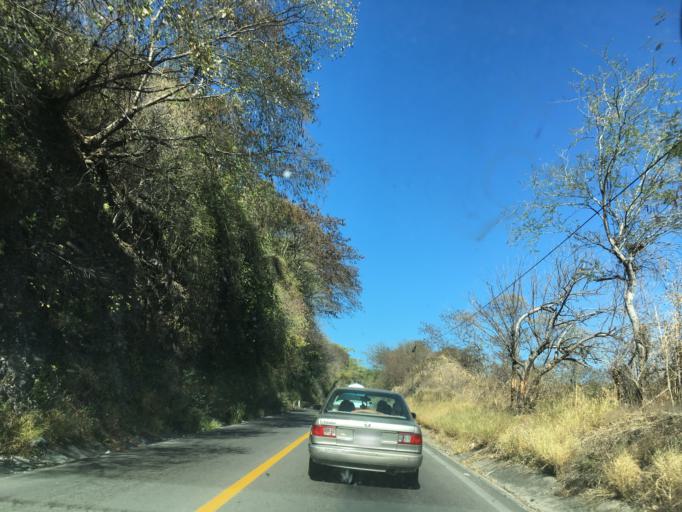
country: MX
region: Michoacan
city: Nueva Italia de Ruiz
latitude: 19.0831
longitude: -102.0618
